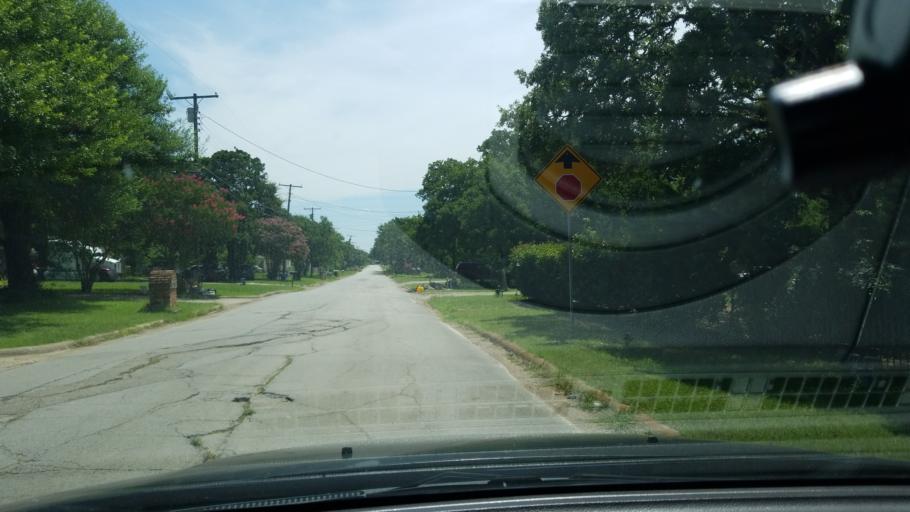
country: US
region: Texas
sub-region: Dallas County
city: Balch Springs
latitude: 32.7523
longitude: -96.6281
